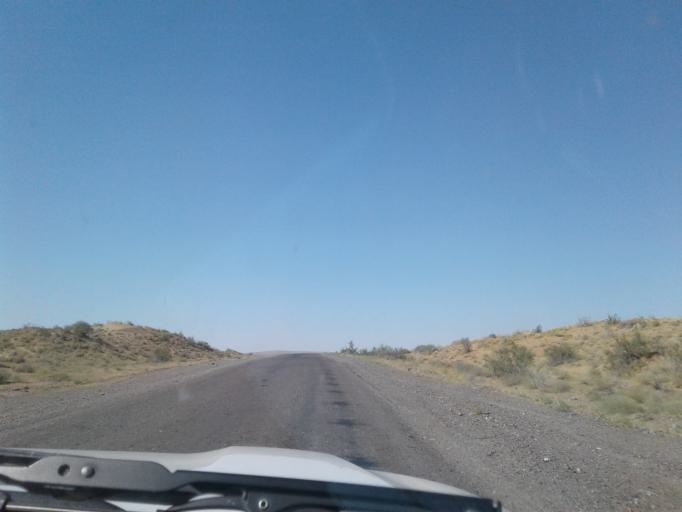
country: TM
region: Mary
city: Yoloeten
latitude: 36.4518
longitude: 62.5894
